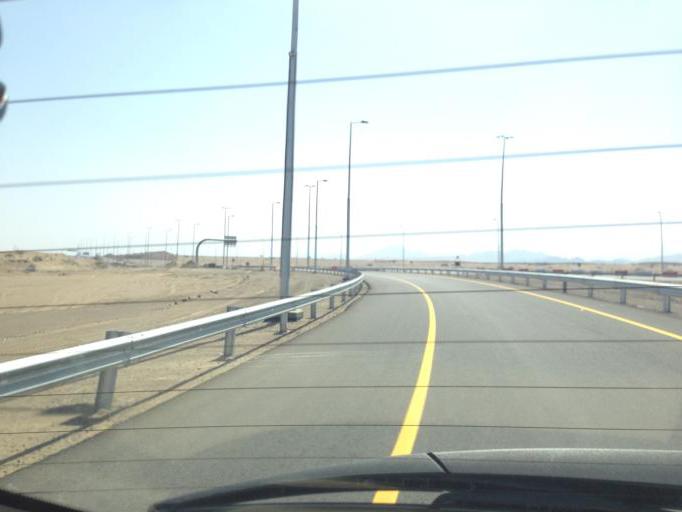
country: OM
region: Al Batinah
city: Rustaq
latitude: 23.5350
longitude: 57.5666
